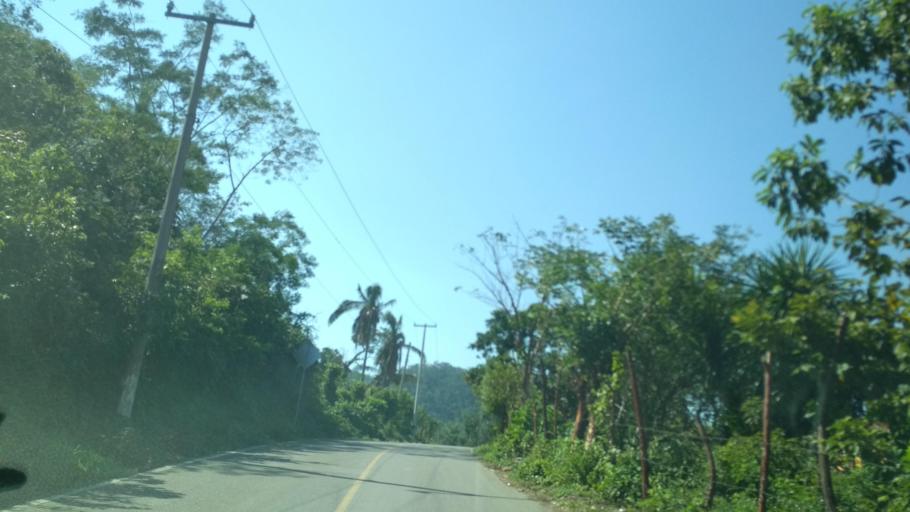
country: MX
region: Veracruz
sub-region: Papantla
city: Polutla
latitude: 20.4741
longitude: -97.2144
